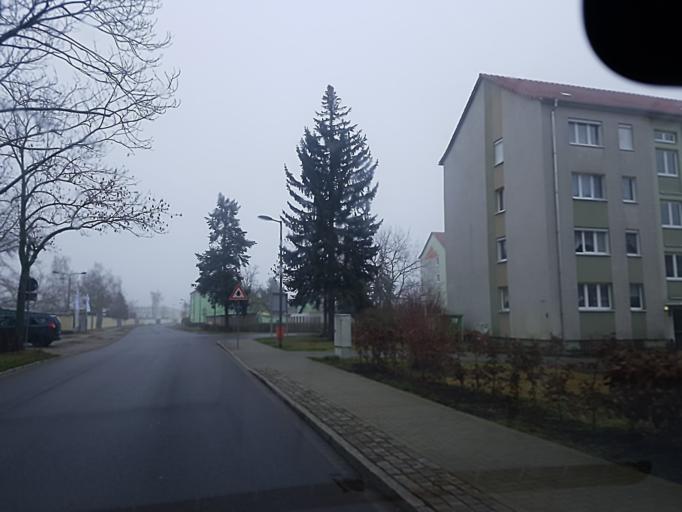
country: DE
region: Brandenburg
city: Finsterwalde
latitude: 51.6337
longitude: 13.7241
